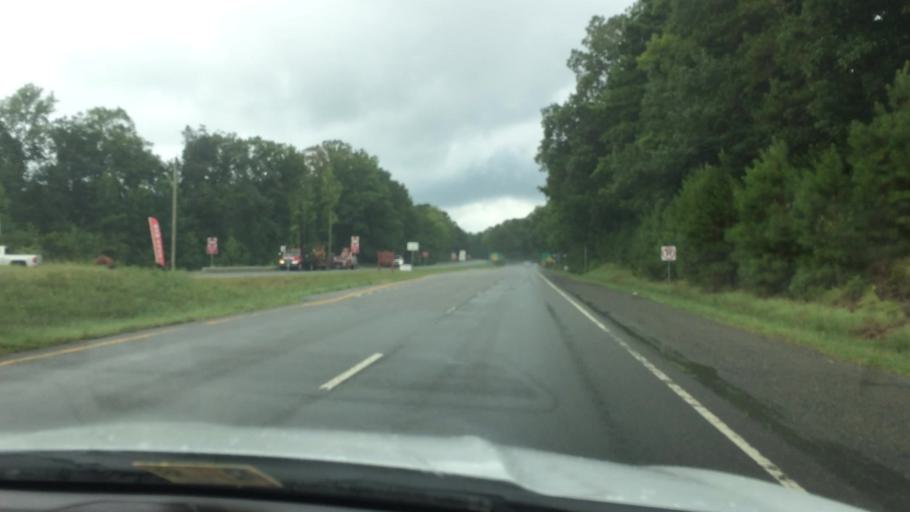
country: US
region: Virginia
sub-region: New Kent County
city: New Kent
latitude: 37.4841
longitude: -76.9117
